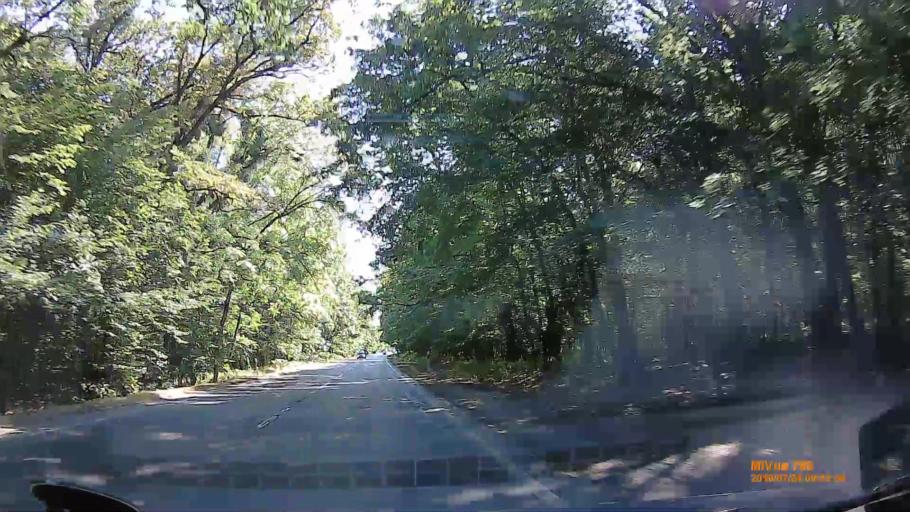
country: HU
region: Szabolcs-Szatmar-Bereg
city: Baktaloranthaza
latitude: 47.9840
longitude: 22.0618
